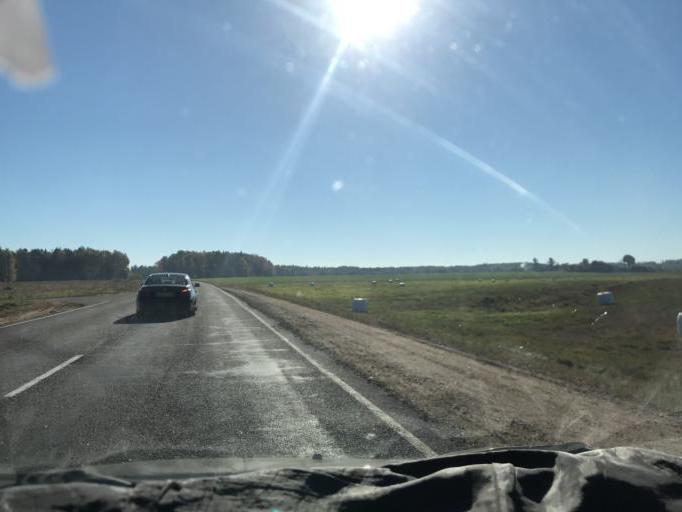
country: BY
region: Mogilev
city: Babruysk
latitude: 53.0615
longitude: 29.0839
